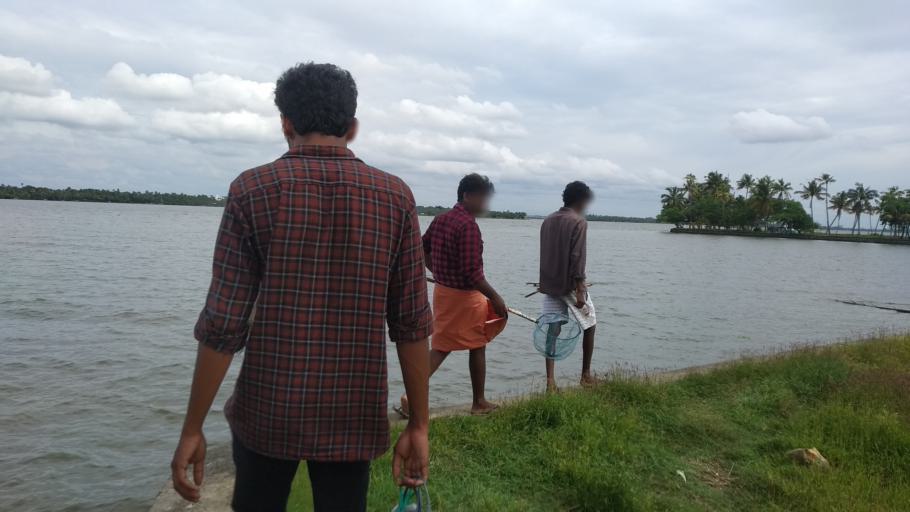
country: IN
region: Kerala
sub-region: Ernakulam
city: Elur
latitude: 10.0825
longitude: 76.2241
